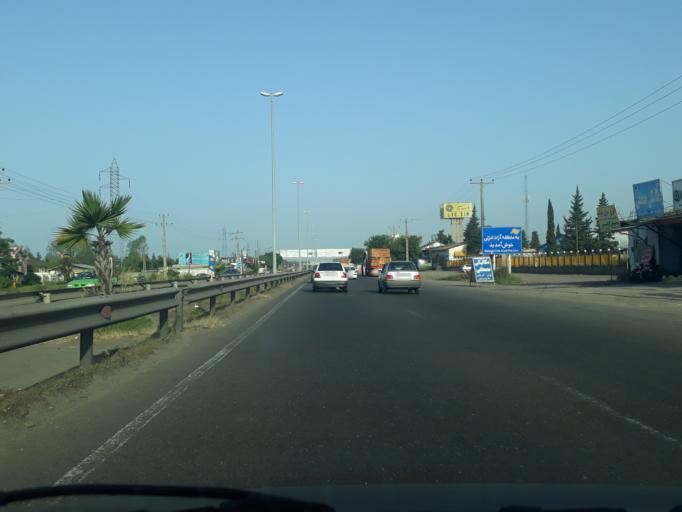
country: IR
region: Gilan
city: Bandar-e Anzali
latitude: 37.4628
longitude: 49.5561
